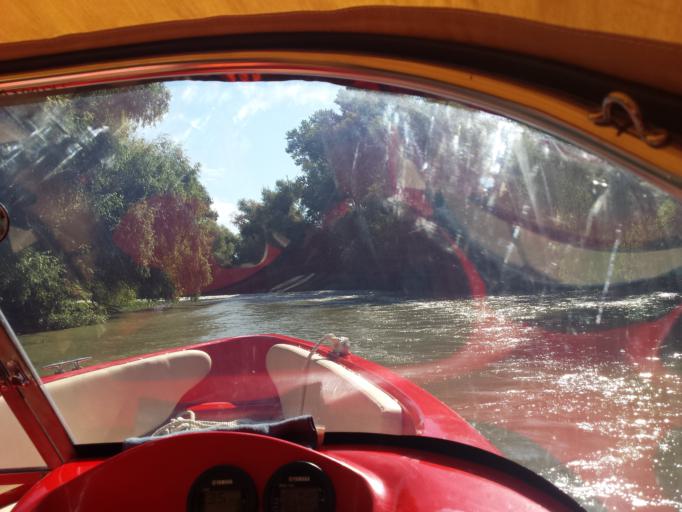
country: RO
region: Tulcea
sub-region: Comuna Pardina
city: Pardina
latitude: 45.2487
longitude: 29.0355
